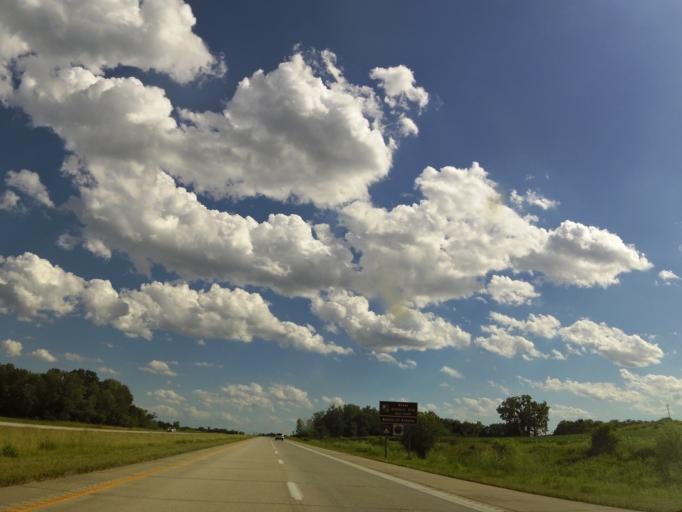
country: US
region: Missouri
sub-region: Clark County
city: Kahoka
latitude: 40.4349
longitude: -91.5696
